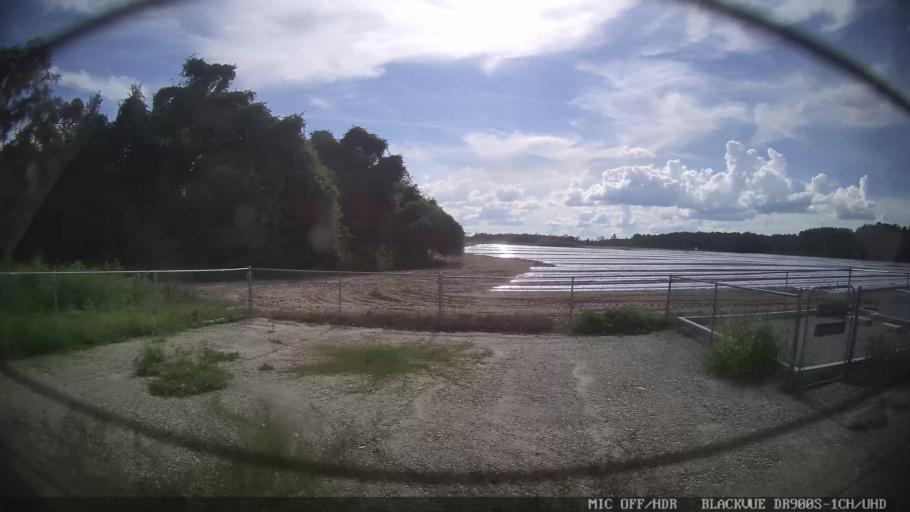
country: US
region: Georgia
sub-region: Echols County
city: Statenville
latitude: 30.6156
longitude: -83.2017
